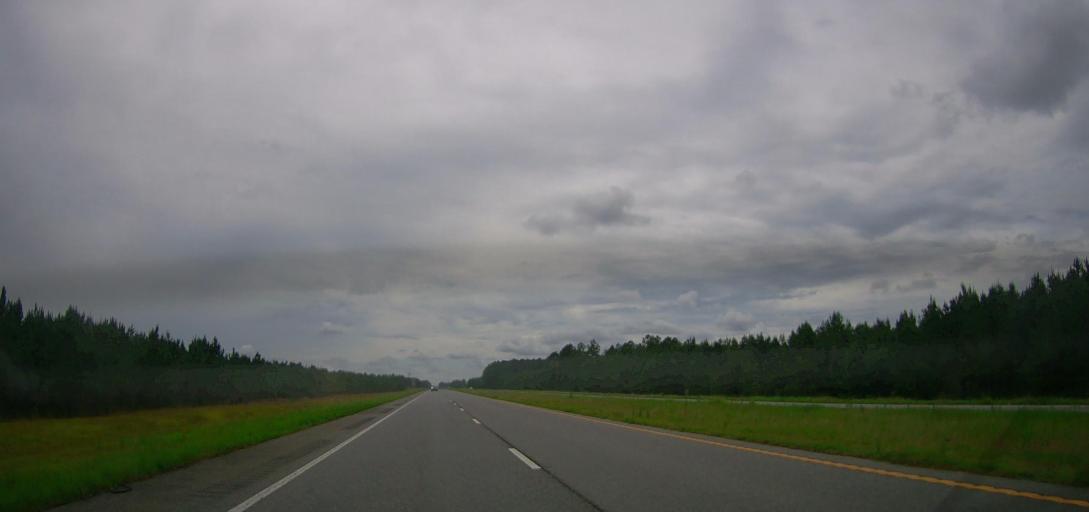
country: US
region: Georgia
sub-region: Appling County
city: Baxley
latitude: 31.7505
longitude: -82.2683
